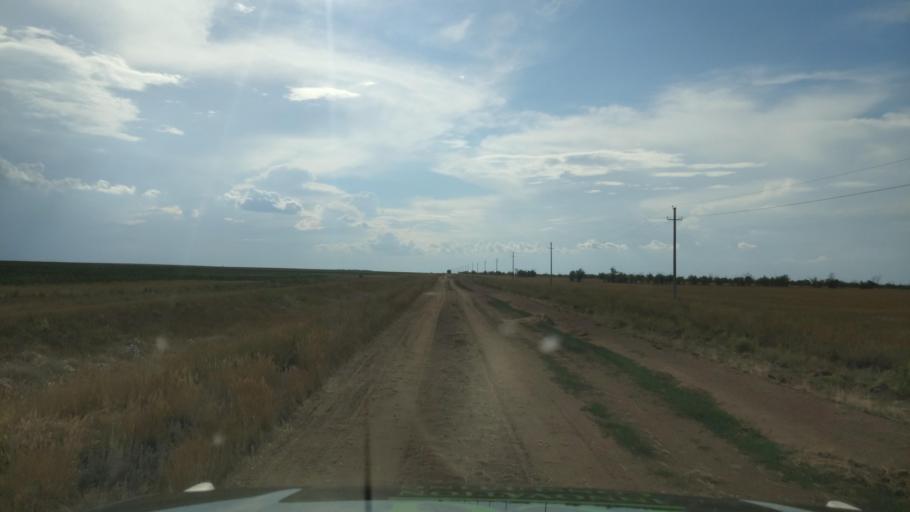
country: KZ
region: Pavlodar
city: Pavlodar
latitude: 52.5126
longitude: 77.4972
